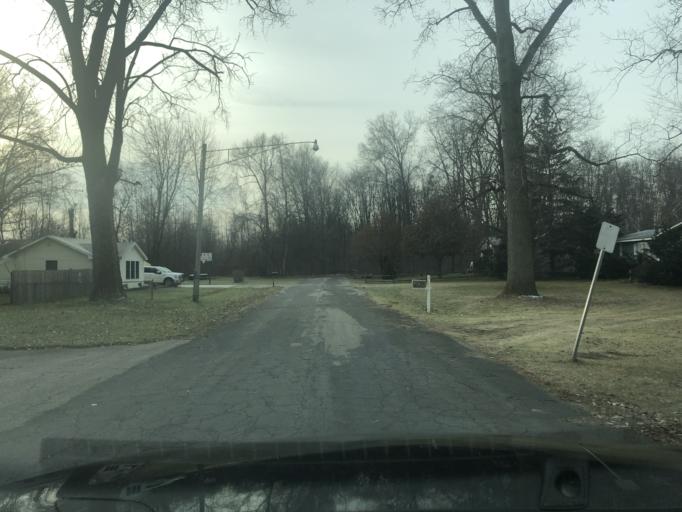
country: US
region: Michigan
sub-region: Wayne County
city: Romulus
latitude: 42.1854
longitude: -83.3268
